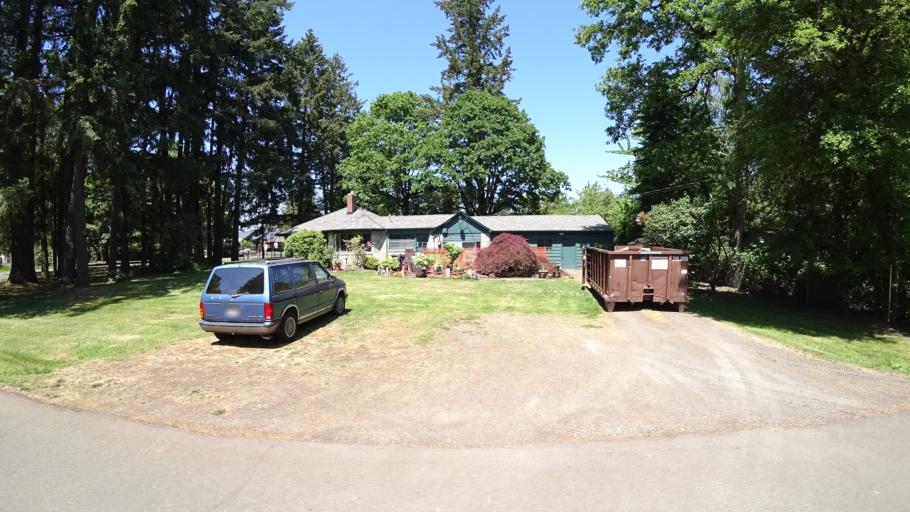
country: US
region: Oregon
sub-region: Washington County
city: Rockcreek
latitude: 45.5247
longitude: -122.9102
